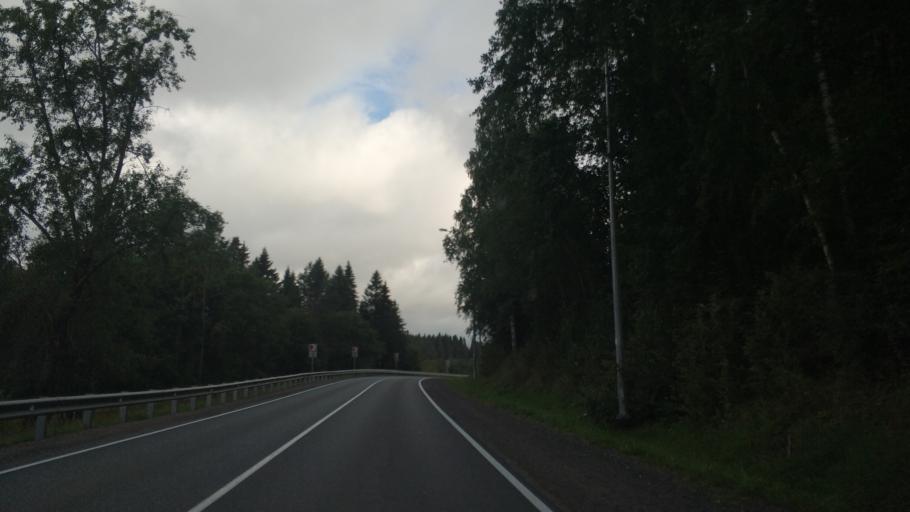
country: RU
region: Republic of Karelia
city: Khelyulya
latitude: 61.7546
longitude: 30.6573
